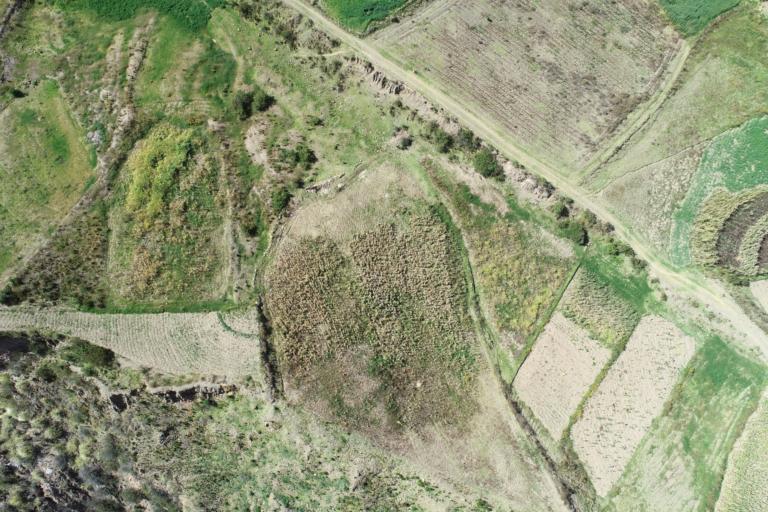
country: BO
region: La Paz
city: La Paz
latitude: -16.5544
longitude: -67.9911
